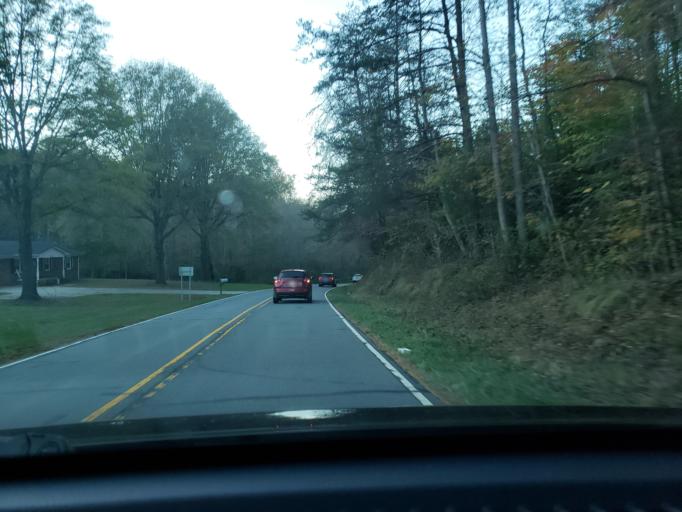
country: US
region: North Carolina
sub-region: Stokes County
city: Danbury
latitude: 36.4209
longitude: -80.2343
